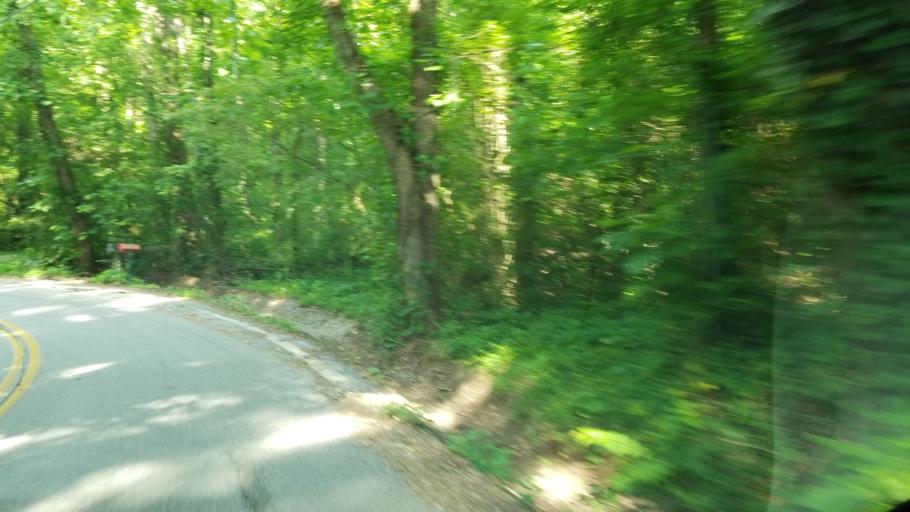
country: US
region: Tennessee
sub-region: Hamilton County
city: Collegedale
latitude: 35.0898
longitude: -85.0270
